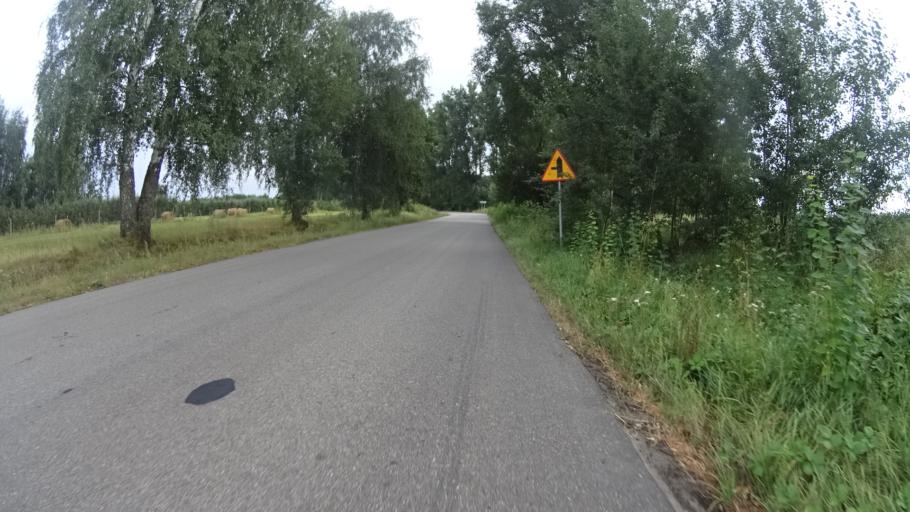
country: PL
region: Masovian Voivodeship
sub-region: Powiat grojecki
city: Goszczyn
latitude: 51.6900
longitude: 20.8577
